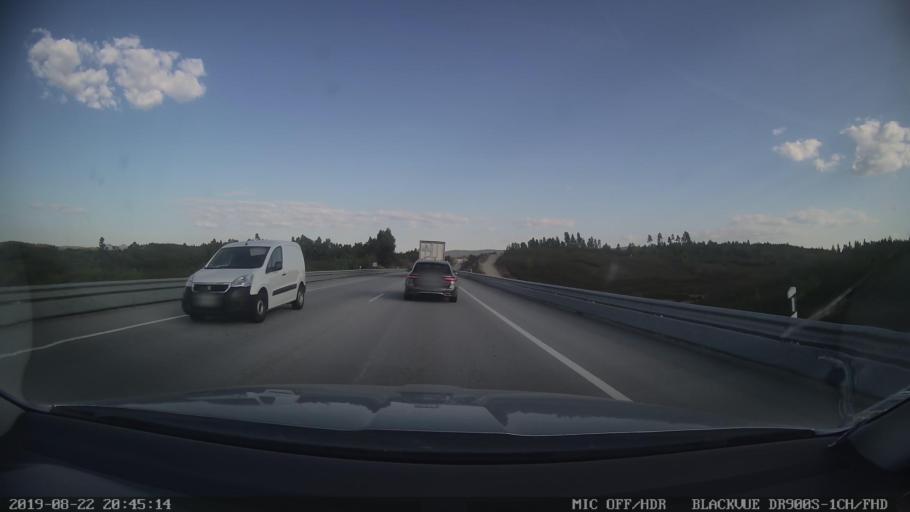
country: PT
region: Castelo Branco
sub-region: Proenca-A-Nova
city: Proenca-a-Nova
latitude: 39.7147
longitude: -7.8640
